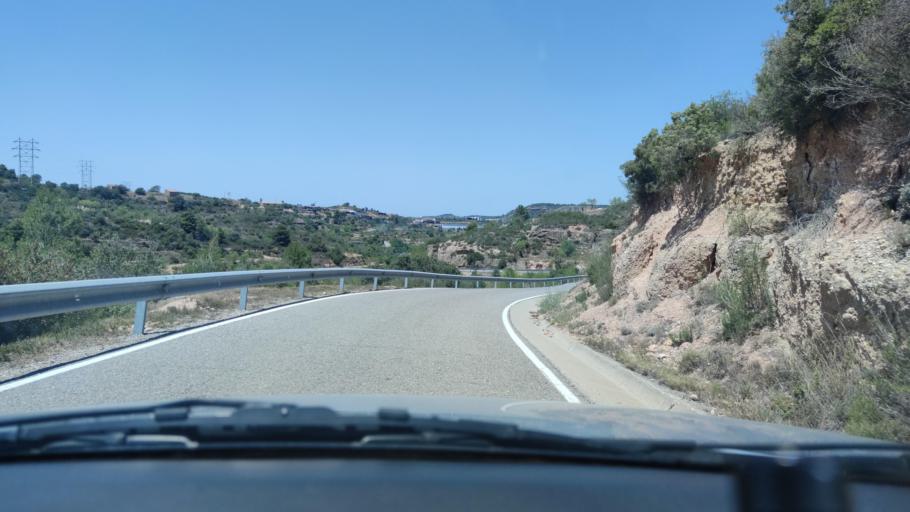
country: ES
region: Catalonia
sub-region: Provincia de Lleida
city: Juncosa
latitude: 41.3644
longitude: 0.7810
